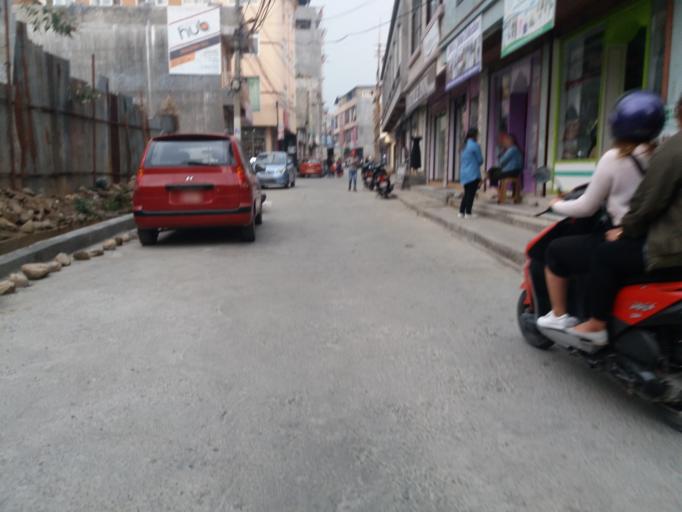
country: NP
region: Western Region
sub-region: Gandaki Zone
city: Pokhara
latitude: 28.2218
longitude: 83.9883
